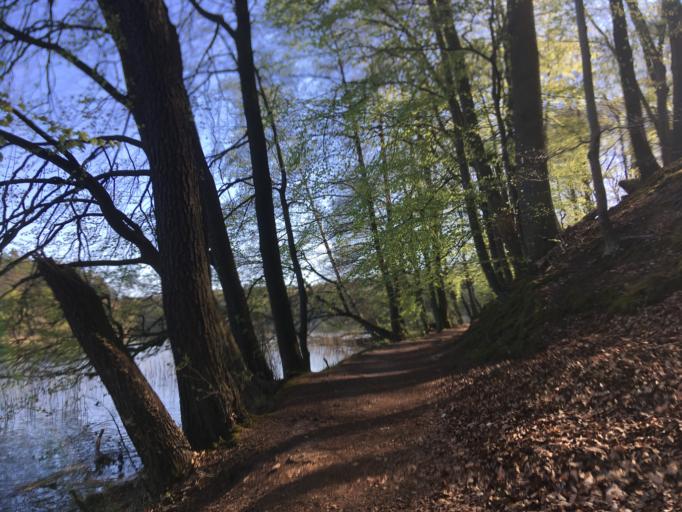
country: DE
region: Brandenburg
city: Wandlitz
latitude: 52.7482
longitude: 13.5226
